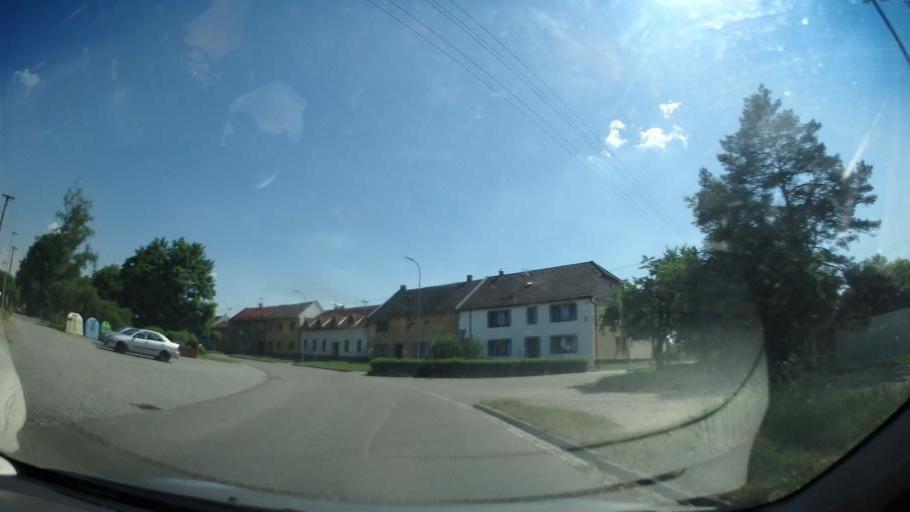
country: CZ
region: Zlin
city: Chropyne
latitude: 49.3594
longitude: 17.3608
